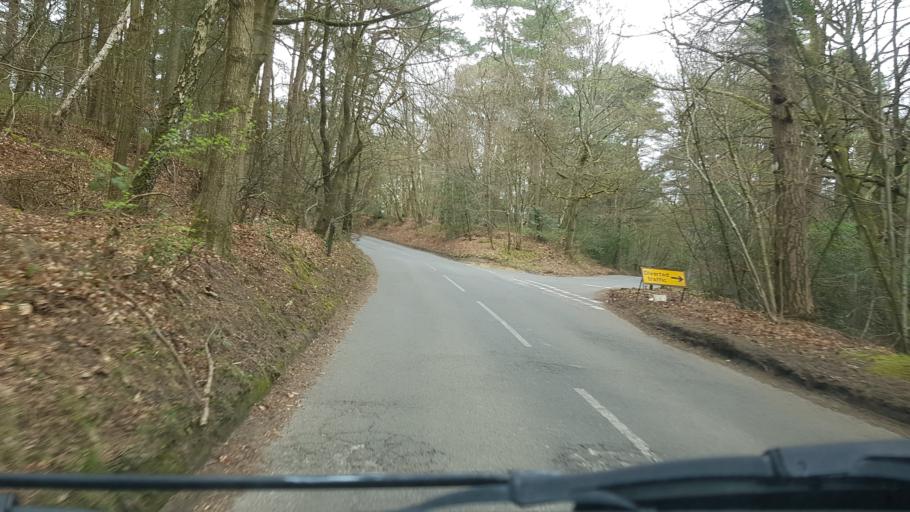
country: GB
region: England
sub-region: Surrey
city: Cranleigh
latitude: 51.1744
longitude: -0.4572
